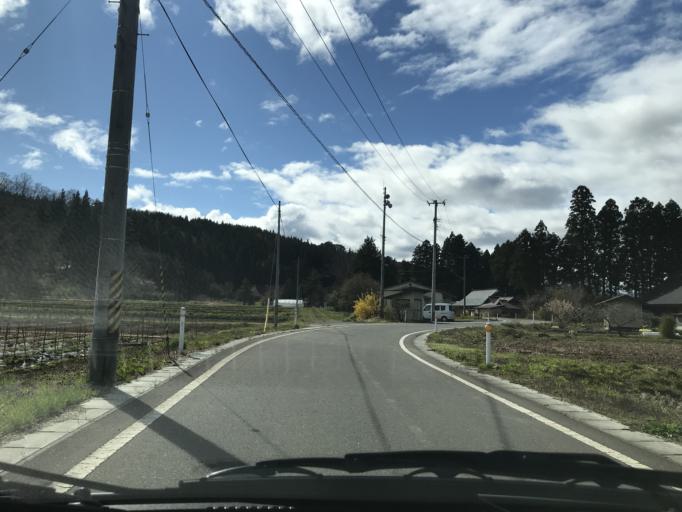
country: JP
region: Iwate
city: Mizusawa
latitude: 39.0804
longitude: 140.9964
